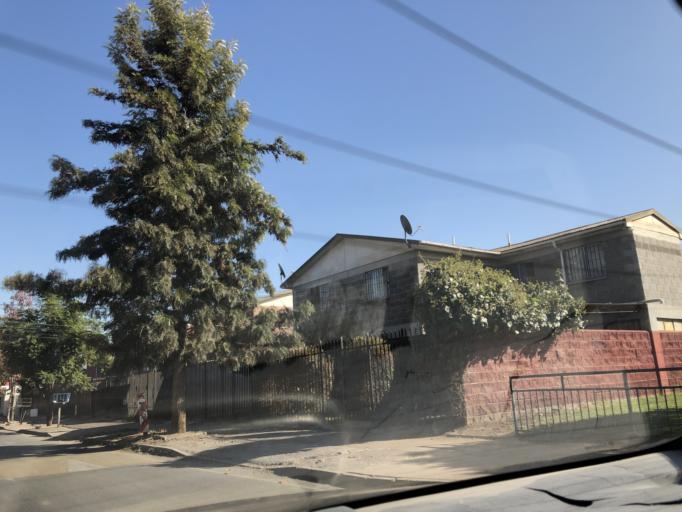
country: CL
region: Santiago Metropolitan
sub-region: Provincia de Santiago
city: La Pintana
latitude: -33.5762
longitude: -70.6024
